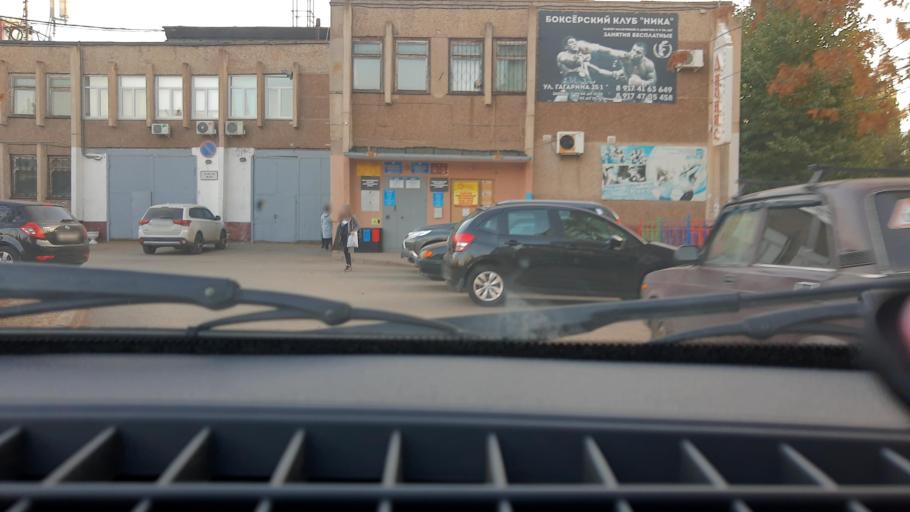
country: RU
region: Bashkortostan
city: Ufa
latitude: 54.7661
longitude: 56.0670
